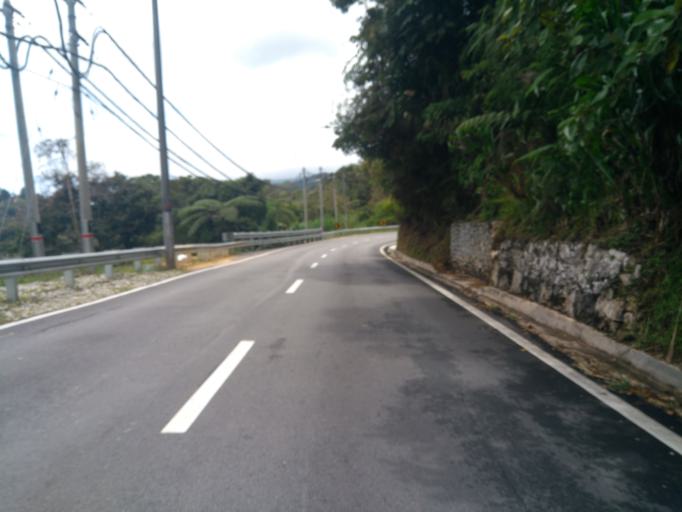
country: MY
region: Pahang
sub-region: Cameron Highlands
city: Tanah Rata
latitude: 4.4783
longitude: 101.3756
